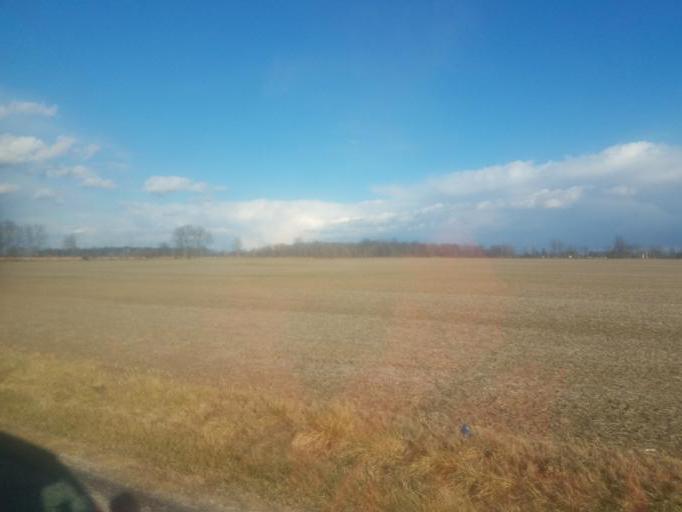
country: US
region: Ohio
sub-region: Marion County
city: Prospect
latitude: 40.3883
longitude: -83.1456
